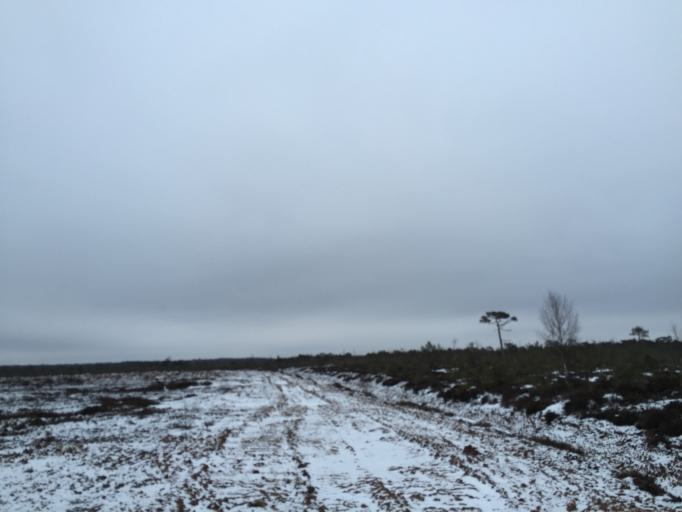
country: LV
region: Saulkrastu
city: Saulkrasti
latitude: 57.2325
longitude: 24.4937
